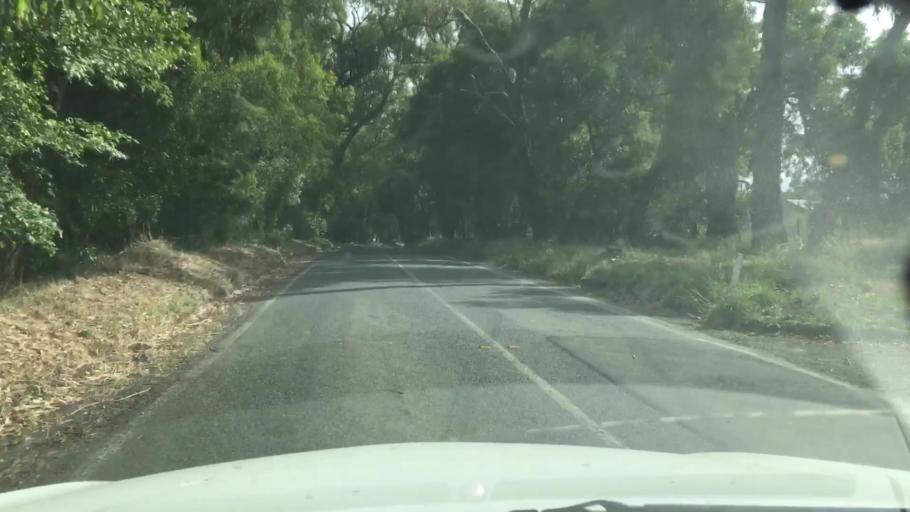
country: AU
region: Victoria
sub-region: Yarra Ranges
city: Woori Yallock
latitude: -37.8184
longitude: 145.4973
